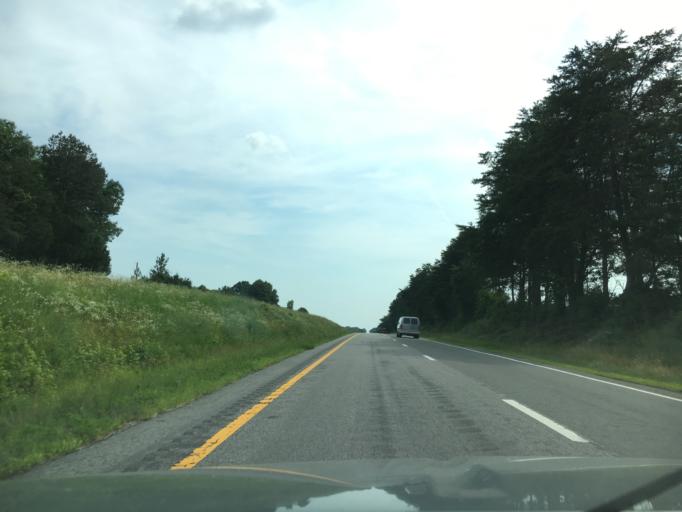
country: US
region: Virginia
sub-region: Mecklenburg County
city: Chase City
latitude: 36.8946
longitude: -78.5450
